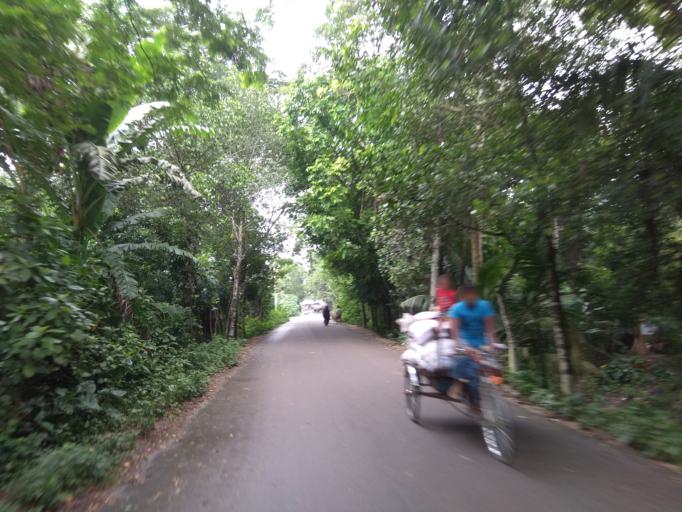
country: BD
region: Dhaka
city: Dohar
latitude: 23.4407
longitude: 90.0720
